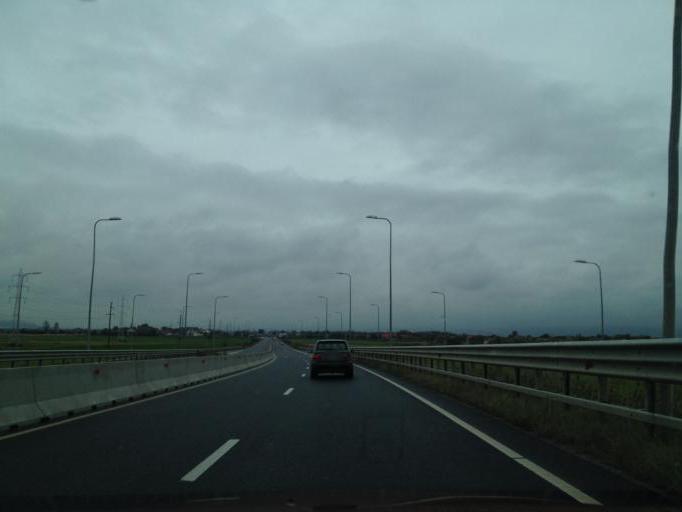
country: RO
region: Brasov
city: Brasov
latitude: 45.6930
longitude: 25.5805
